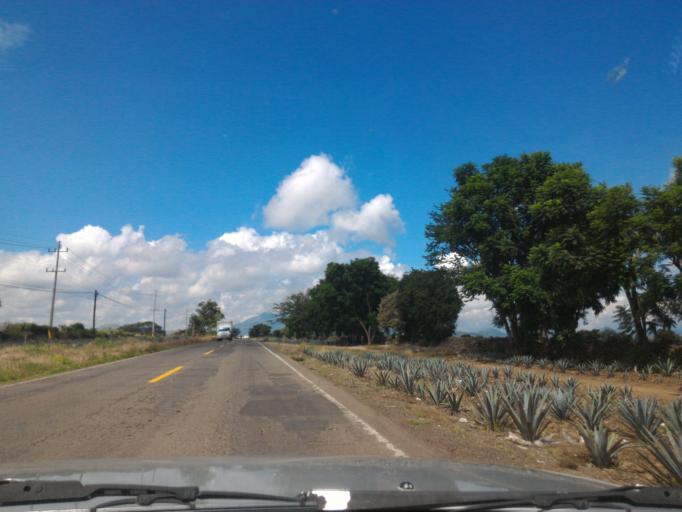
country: MX
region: Jalisco
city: Tequila
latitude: 20.8715
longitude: -103.7970
